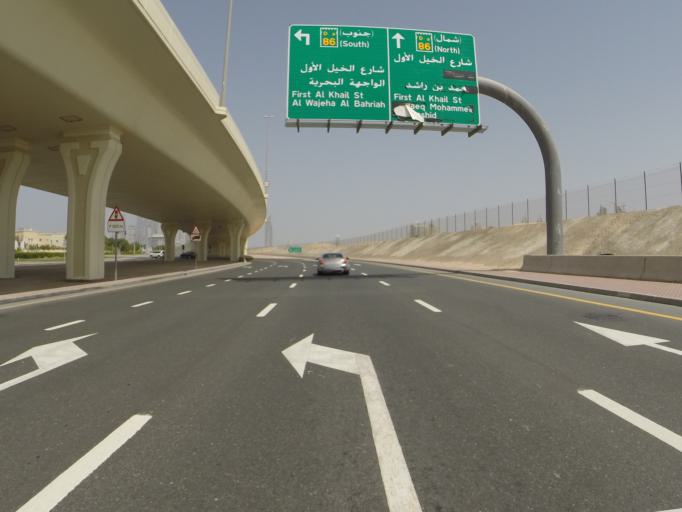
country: AE
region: Dubai
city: Dubai
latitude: 25.0788
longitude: 55.1800
